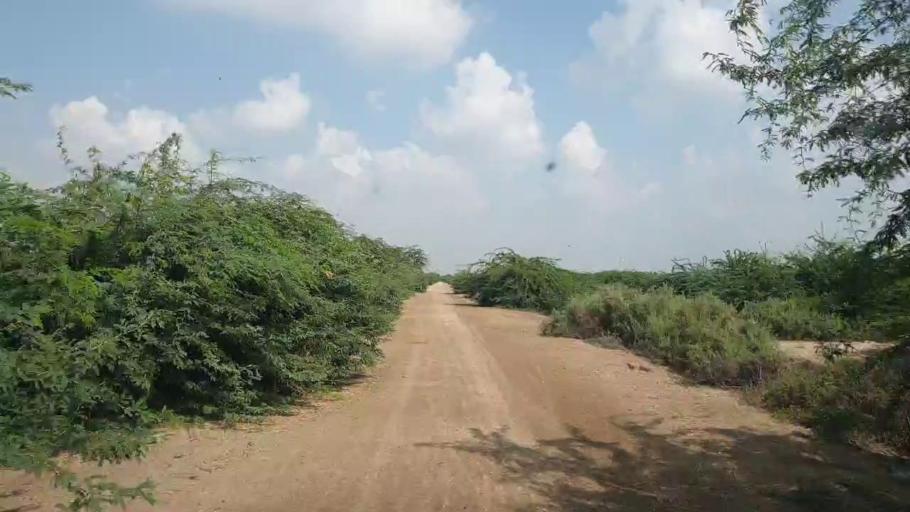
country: PK
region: Sindh
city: Badin
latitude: 24.4906
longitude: 68.6532
